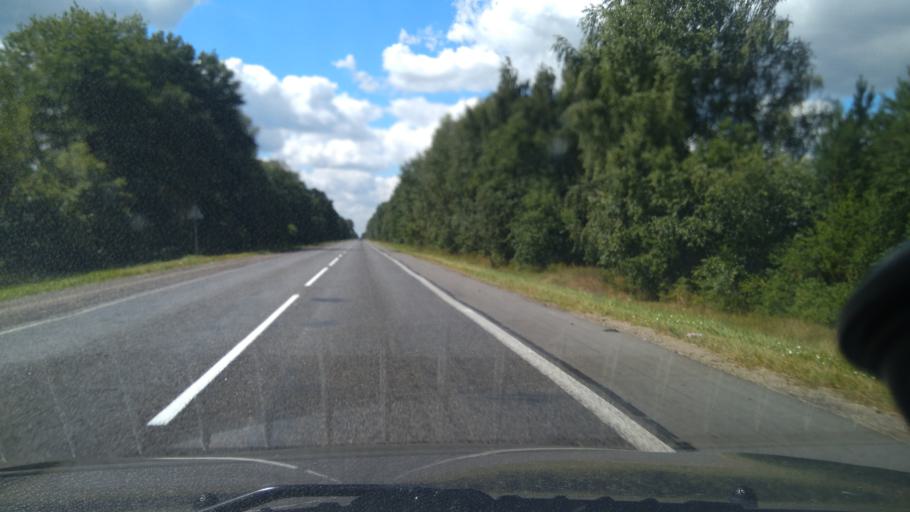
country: BY
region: Brest
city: Ivatsevichy
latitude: 52.6813
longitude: 25.2810
